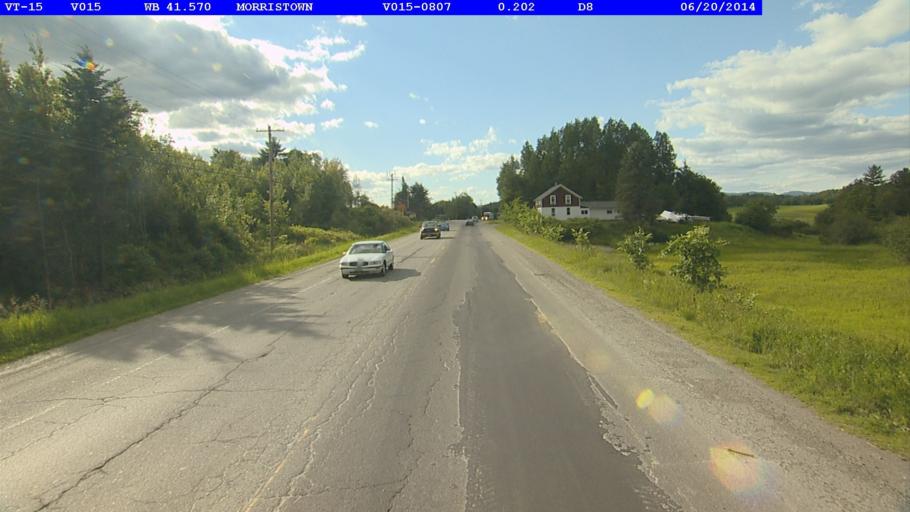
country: US
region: Vermont
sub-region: Lamoille County
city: Hyde Park
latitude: 44.5834
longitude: -72.5998
